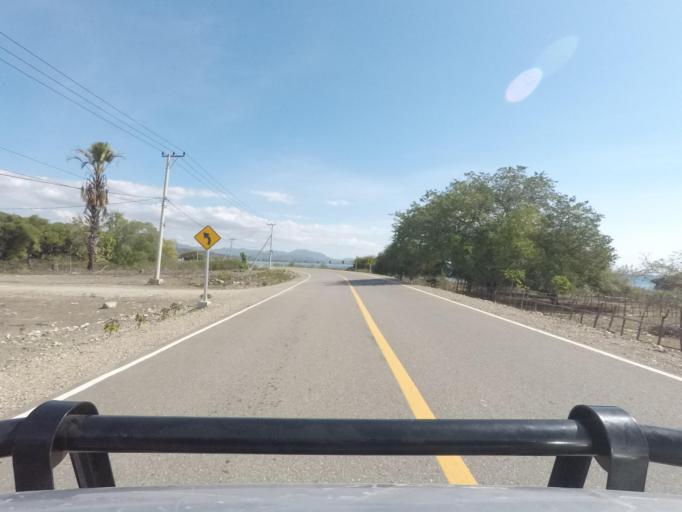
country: ID
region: East Nusa Tenggara
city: Atambua
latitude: -8.9302
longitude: 124.9819
